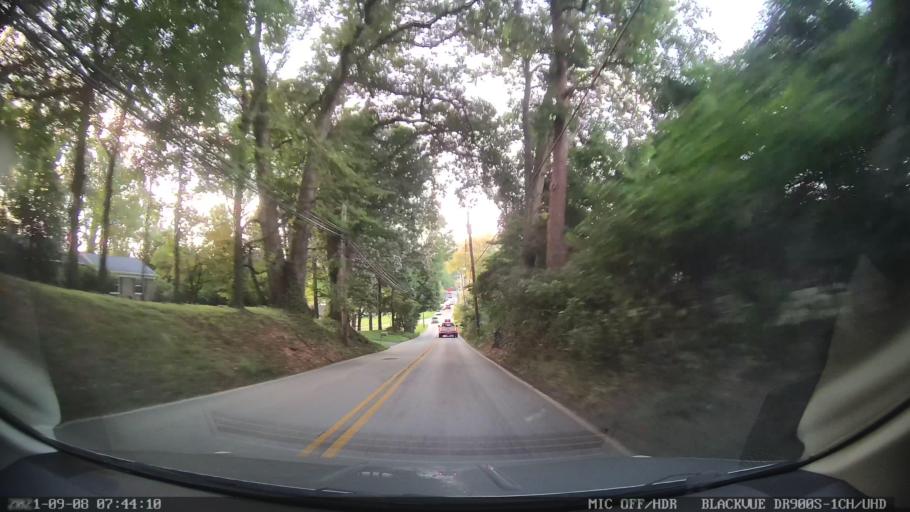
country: US
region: Pennsylvania
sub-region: Delaware County
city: Radnor
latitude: 40.0629
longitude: -75.3745
